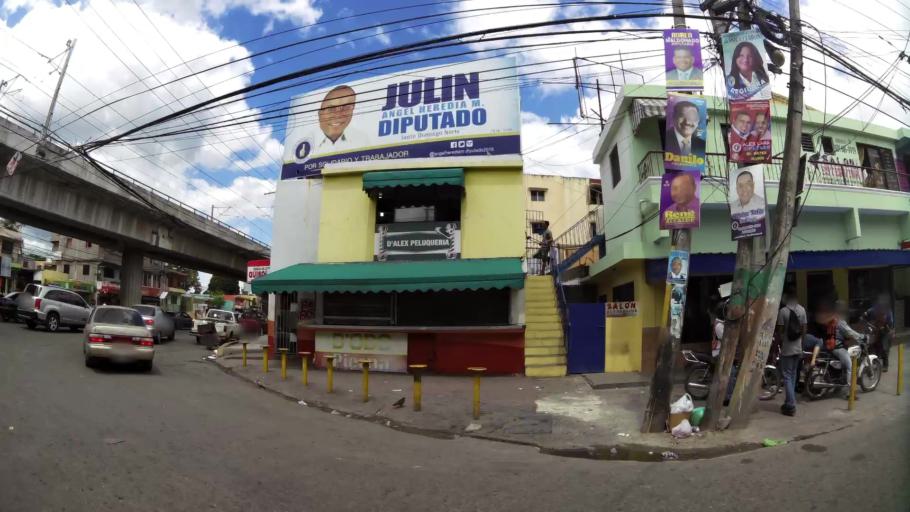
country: DO
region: Nacional
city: Ensanche Luperon
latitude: 18.5312
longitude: -69.9072
